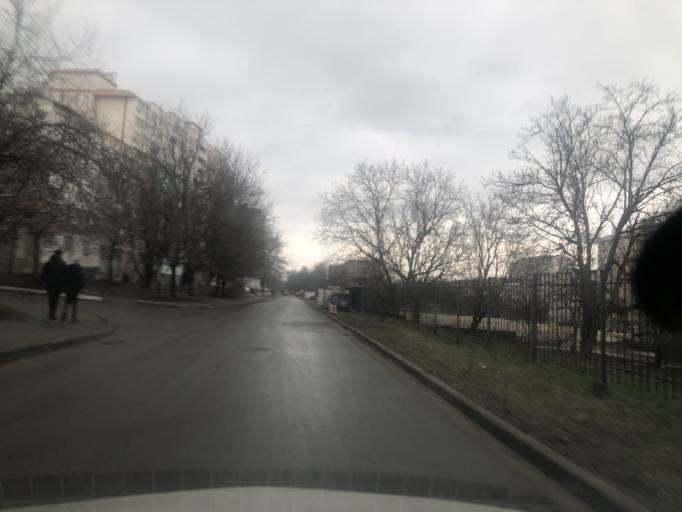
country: MD
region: Chisinau
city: Stauceni
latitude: 47.0641
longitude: 28.8429
